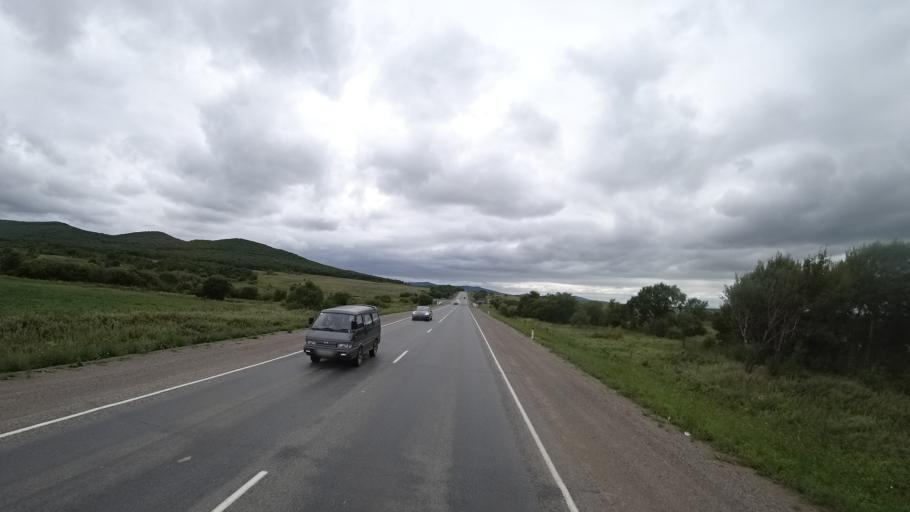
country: RU
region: Primorskiy
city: Chernigovka
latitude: 44.3103
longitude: 132.5450
